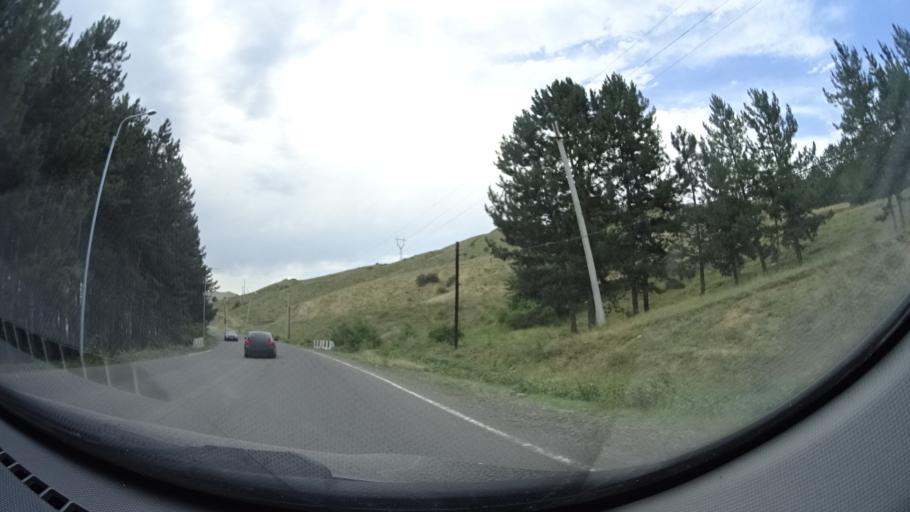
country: GE
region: Samtskhe-Javakheti
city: Aspindza
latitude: 41.5844
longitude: 43.2441
